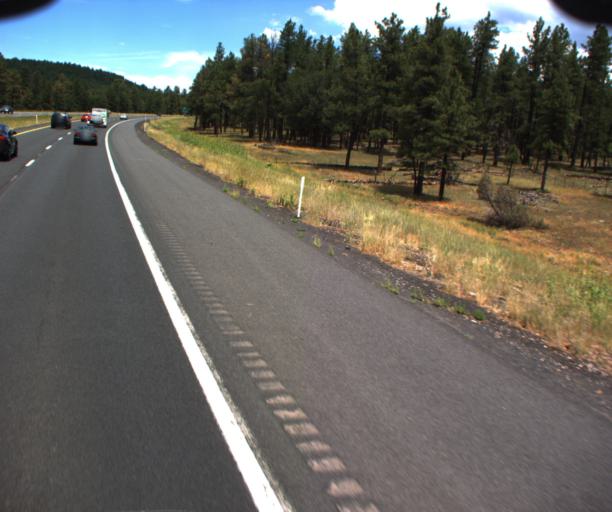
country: US
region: Arizona
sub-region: Coconino County
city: Sedona
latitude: 34.9571
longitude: -111.6770
